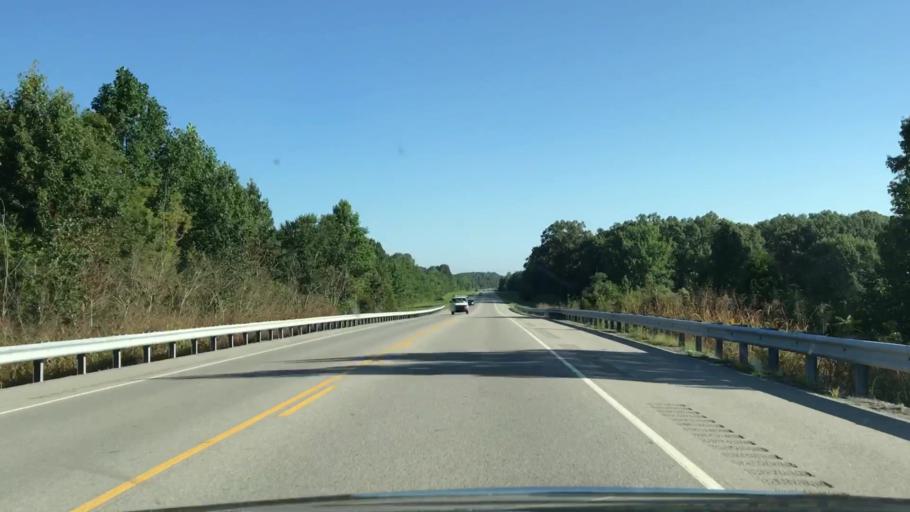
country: US
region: Tennessee
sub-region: Putnam County
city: Baxter
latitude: 36.1611
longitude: -85.6281
